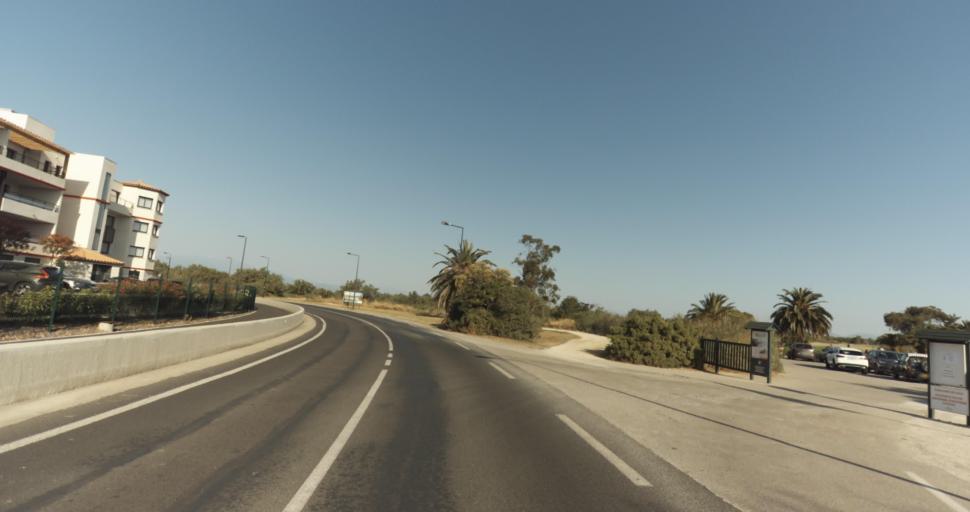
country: FR
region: Languedoc-Roussillon
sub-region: Departement des Pyrenees-Orientales
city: Saint-Cyprien-Plage
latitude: 42.6396
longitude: 3.0174
